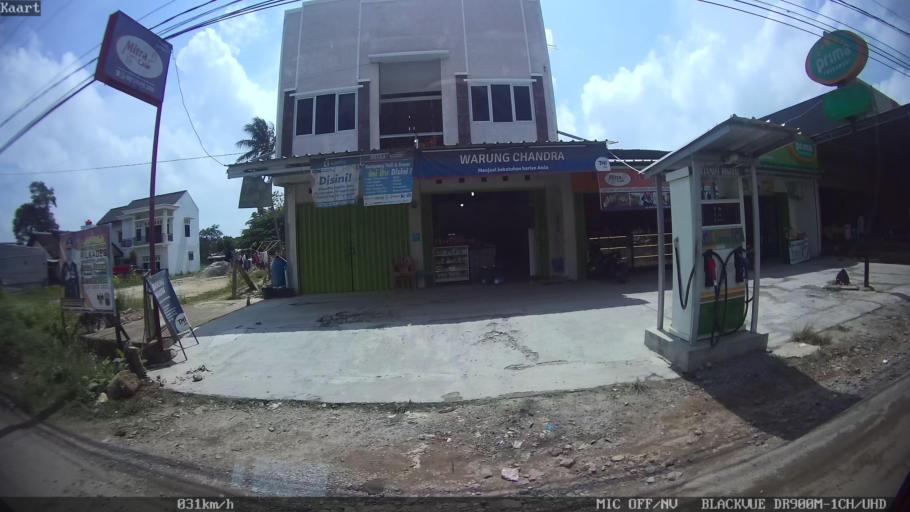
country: ID
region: Lampung
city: Kedaton
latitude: -5.3514
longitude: 105.2994
